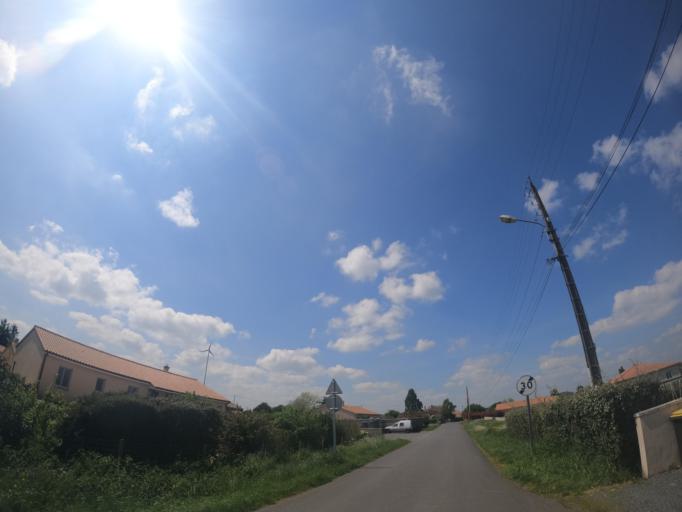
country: FR
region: Poitou-Charentes
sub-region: Departement des Deux-Sevres
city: Saint-Varent
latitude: 46.8592
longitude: -0.2423
